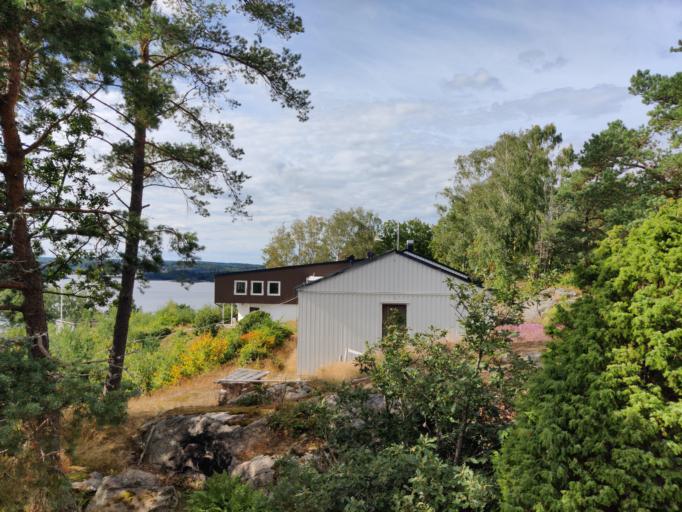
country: SE
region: Vaestra Goetaland
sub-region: Uddevalla Kommun
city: Ljungskile
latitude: 58.2170
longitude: 11.8862
